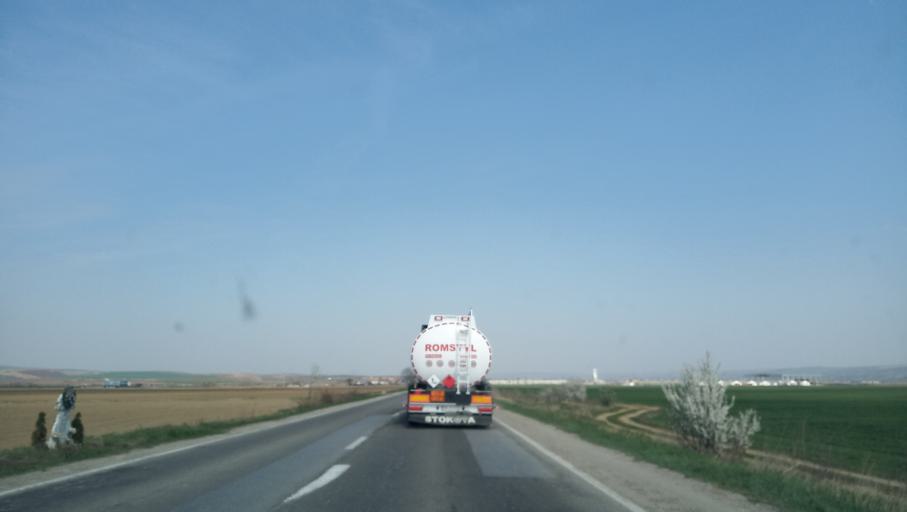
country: RO
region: Alba
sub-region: Comuna Santimbru
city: Santimbru
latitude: 46.1691
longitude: 23.6501
